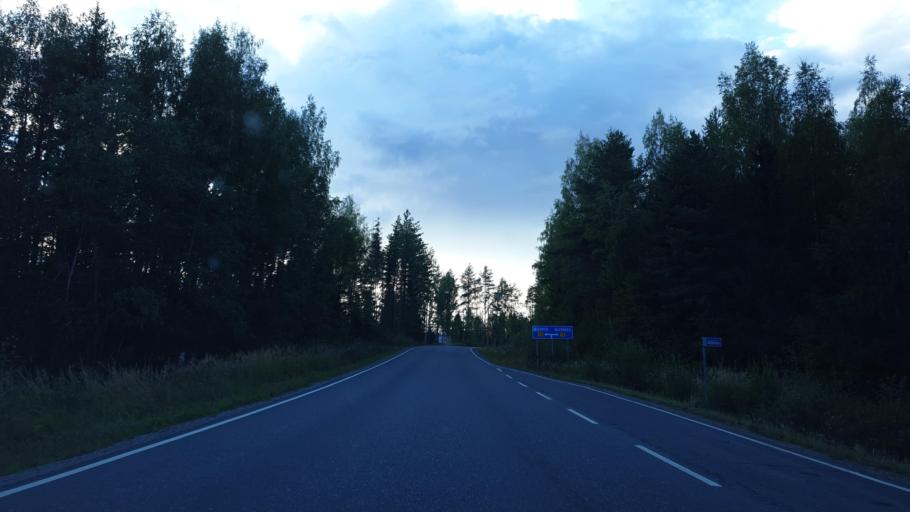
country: FI
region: Northern Savo
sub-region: Koillis-Savo
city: Juankoski
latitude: 63.2026
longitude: 28.2845
